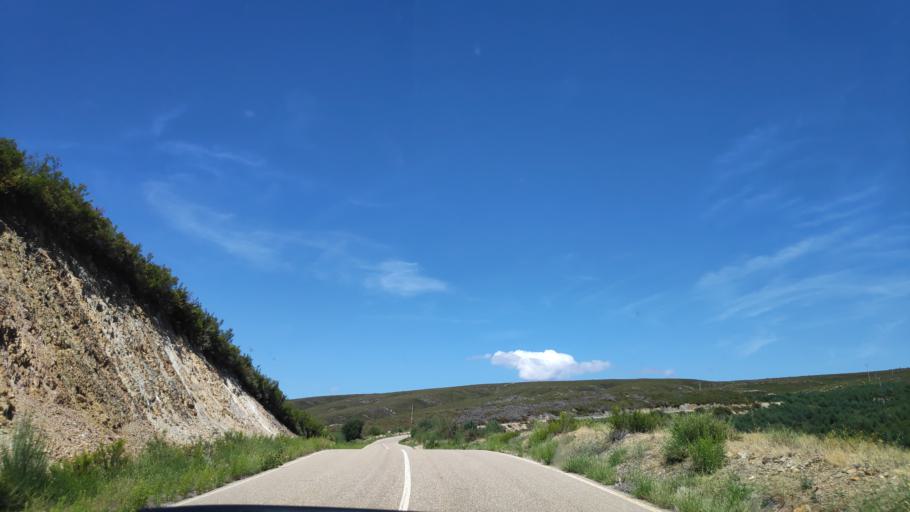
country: ES
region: Castille and Leon
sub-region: Provincia de Zamora
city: Requejo
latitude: 42.0019
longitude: -6.6933
